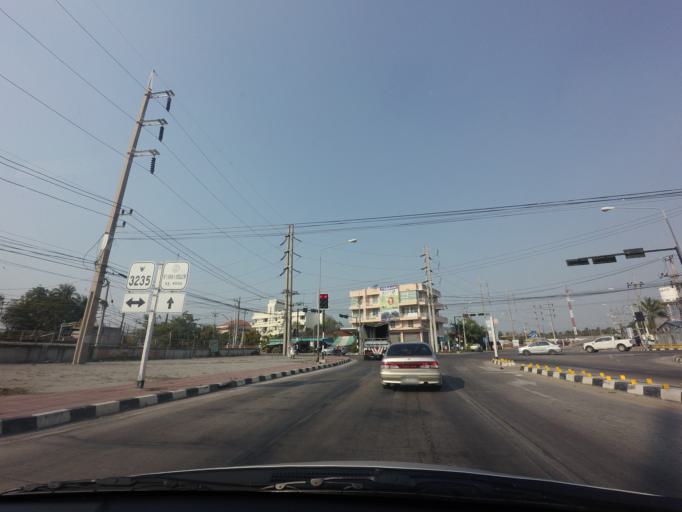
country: TH
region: Nakhon Pathom
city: Nakhon Chai Si
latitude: 13.7906
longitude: 100.1957
